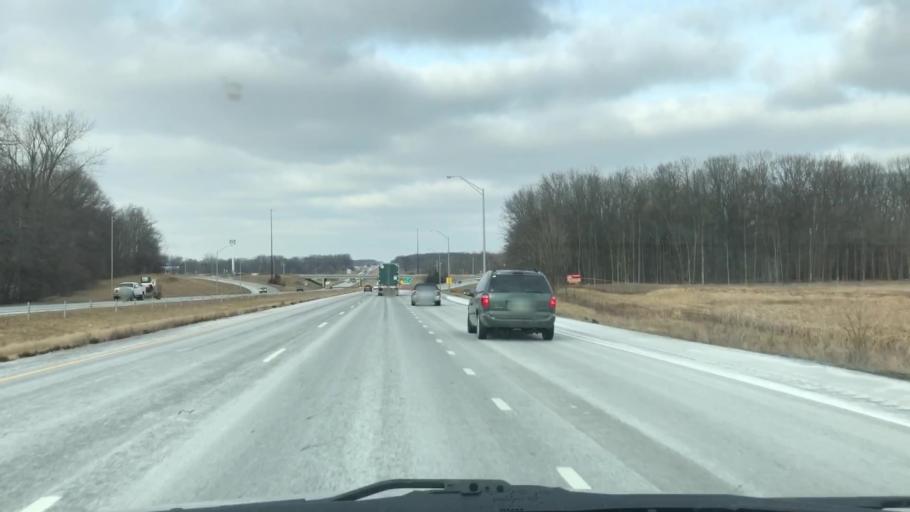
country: US
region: Indiana
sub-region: DeKalb County
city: Waterloo
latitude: 41.4352
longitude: -85.0534
